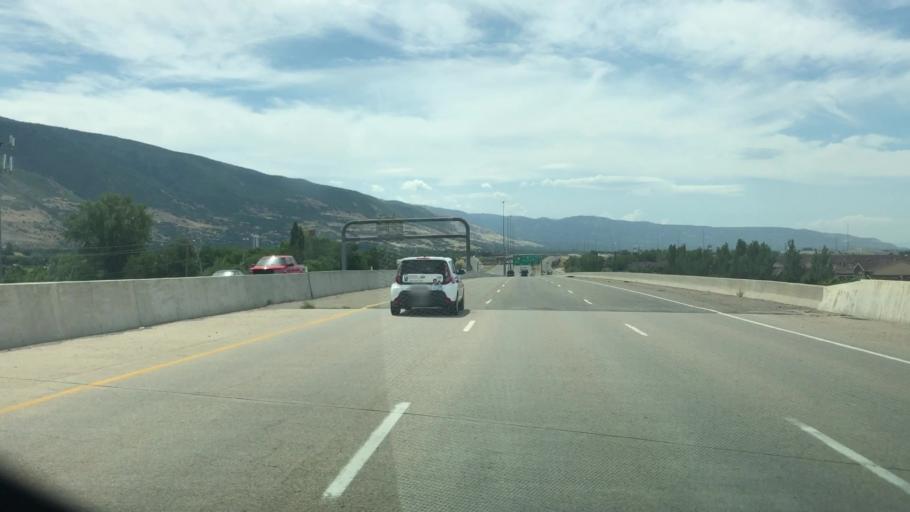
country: US
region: Utah
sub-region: Davis County
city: Farmington
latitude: 41.0014
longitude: -111.9074
